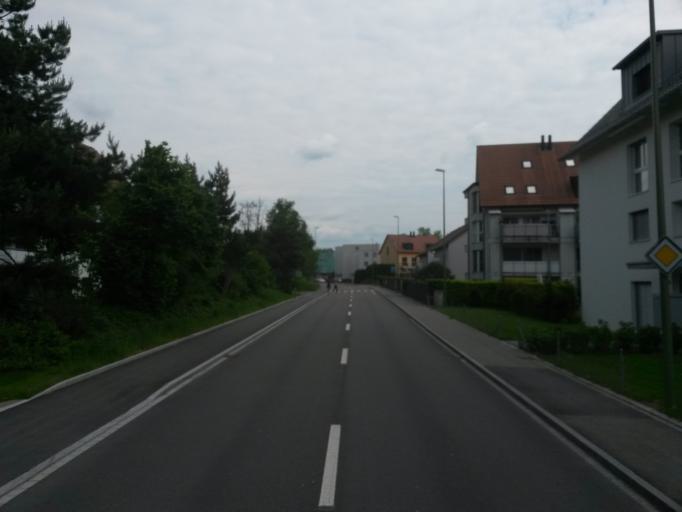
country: CH
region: Zurich
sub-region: Bezirk Pfaeffikon
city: Fehraltorf
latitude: 47.3859
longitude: 8.7563
